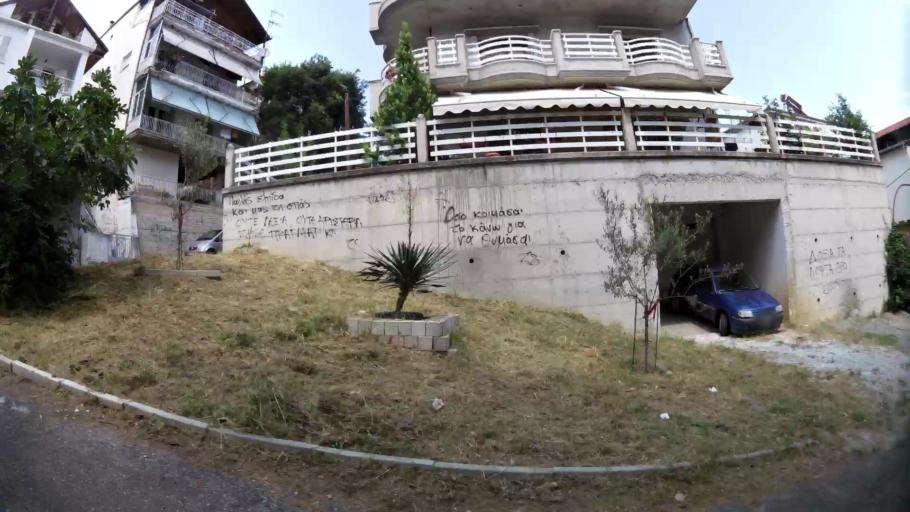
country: GR
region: Central Macedonia
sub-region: Nomos Imathias
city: Veroia
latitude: 40.5201
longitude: 22.2069
